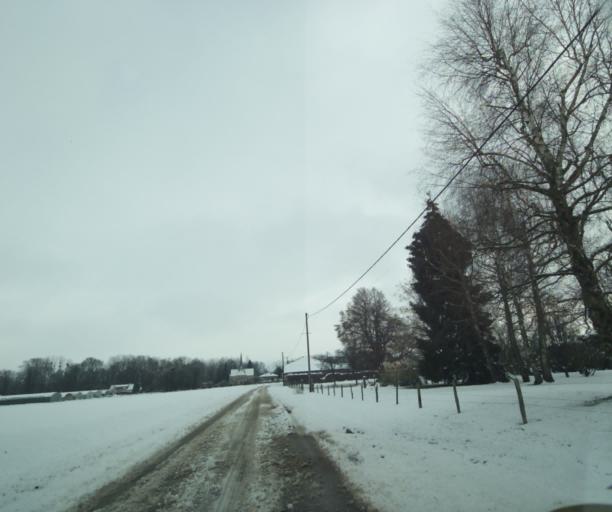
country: FR
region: Champagne-Ardenne
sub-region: Departement de la Haute-Marne
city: Montier-en-Der
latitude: 48.4967
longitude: 4.6968
